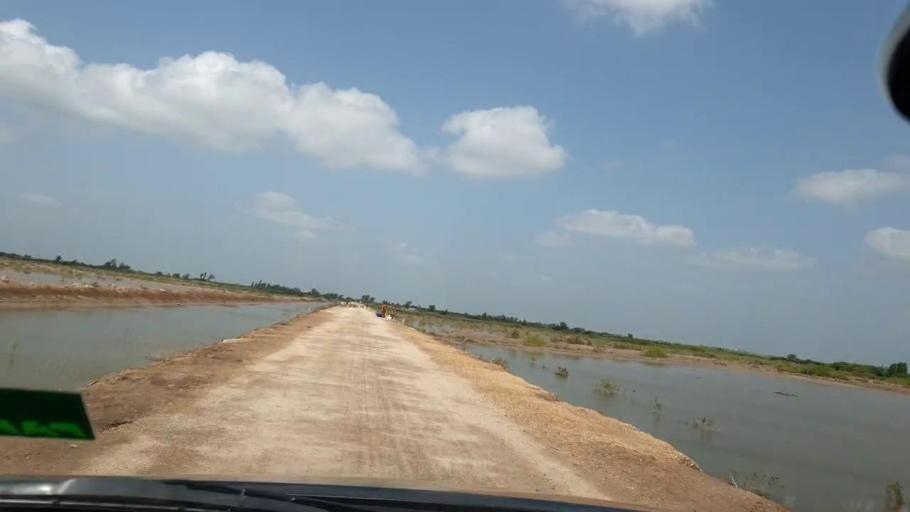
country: PK
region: Sindh
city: Kadhan
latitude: 24.5972
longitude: 69.1283
